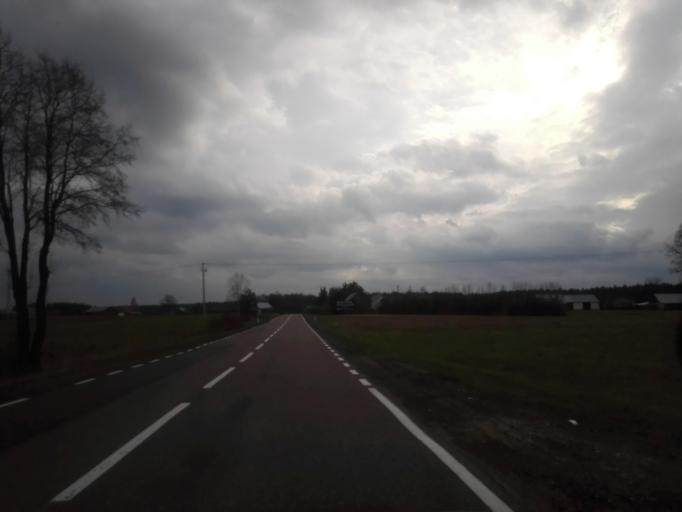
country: PL
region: Podlasie
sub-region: Powiat sejnenski
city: Krasnopol
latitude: 53.9429
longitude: 23.1856
